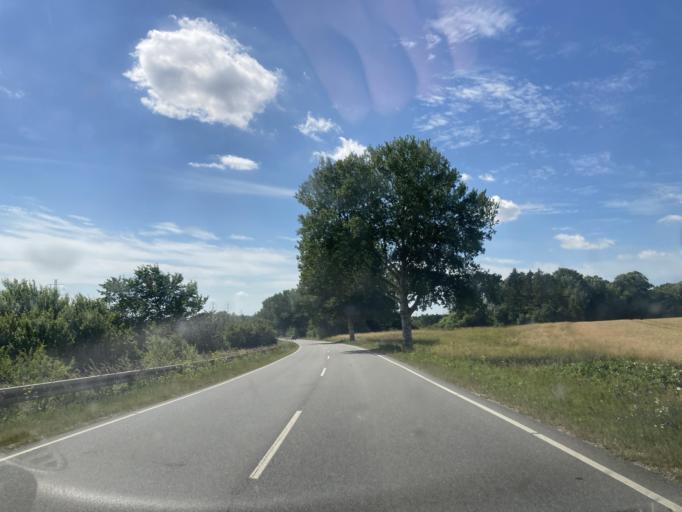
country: DK
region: Zealand
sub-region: Koge Kommune
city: Ejby
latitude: 55.4948
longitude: 12.0968
